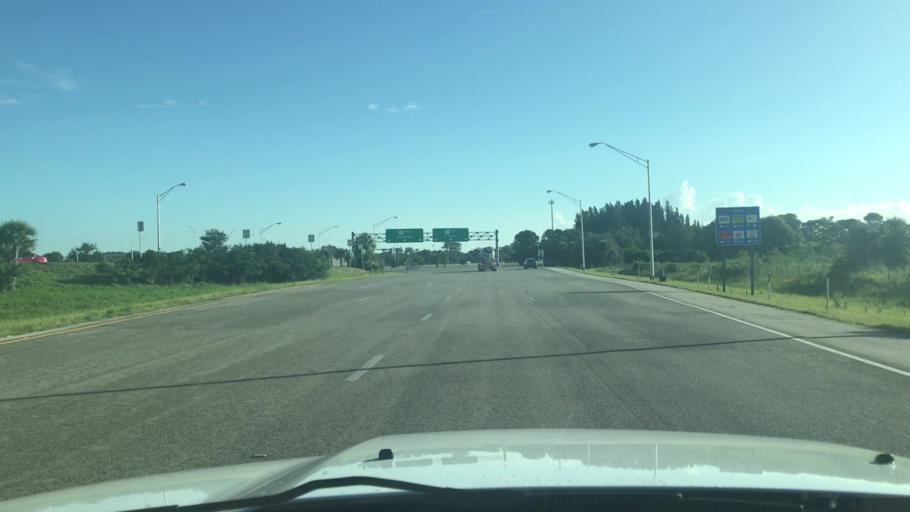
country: US
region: Florida
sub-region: Saint Lucie County
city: Fort Pierce South
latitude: 27.4138
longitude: -80.3869
